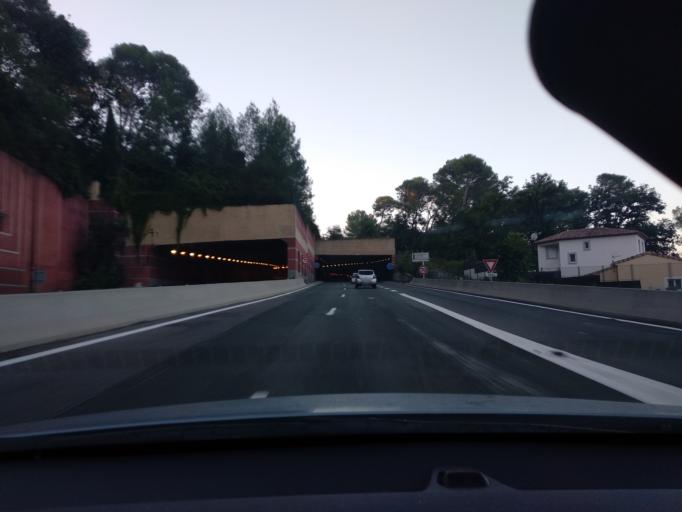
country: FR
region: Provence-Alpes-Cote d'Azur
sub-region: Departement des Alpes-Maritimes
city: Grasse
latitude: 43.6402
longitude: 6.9361
